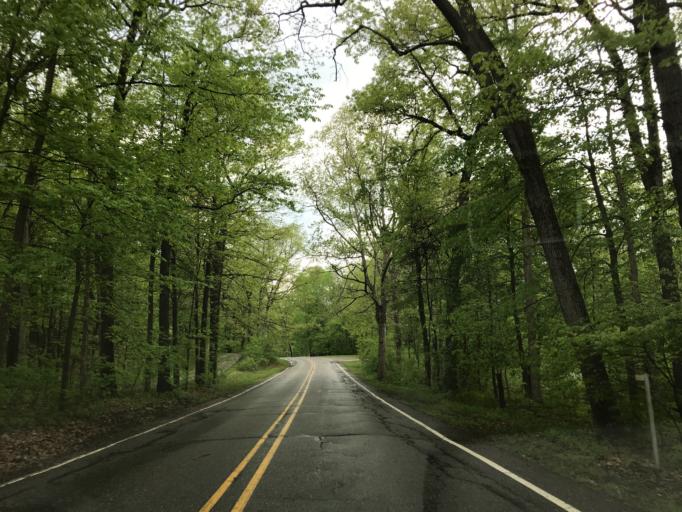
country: US
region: Michigan
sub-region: Oakland County
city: South Lyon
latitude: 42.5340
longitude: -83.6546
